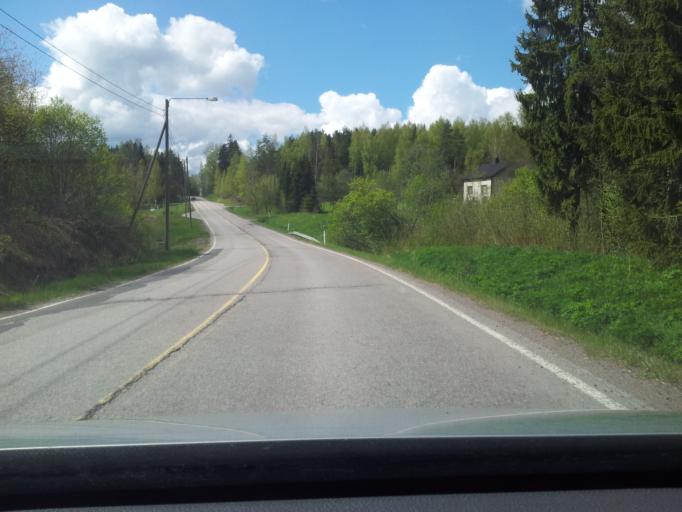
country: FI
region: Uusimaa
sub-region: Loviisa
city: Perna
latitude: 60.4962
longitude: 25.9099
